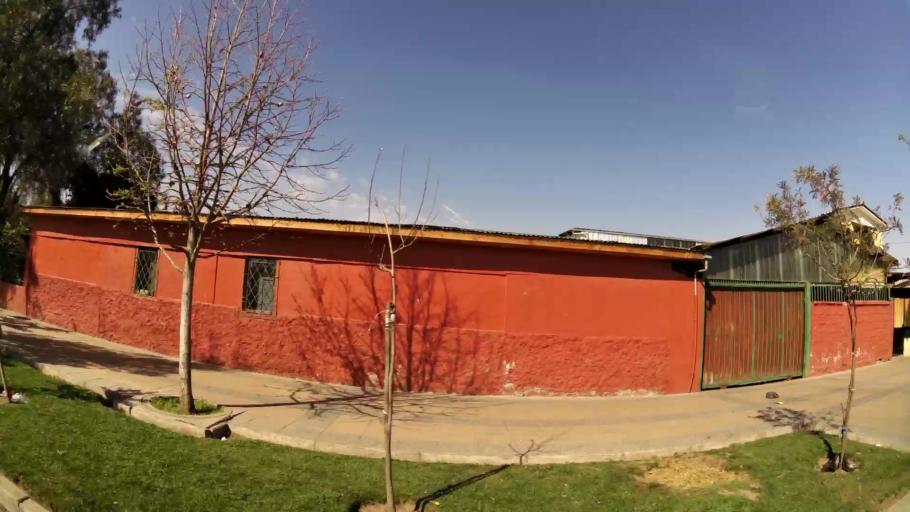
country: CL
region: Santiago Metropolitan
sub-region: Provincia de Santiago
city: La Pintana
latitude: -33.5325
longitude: -70.6164
